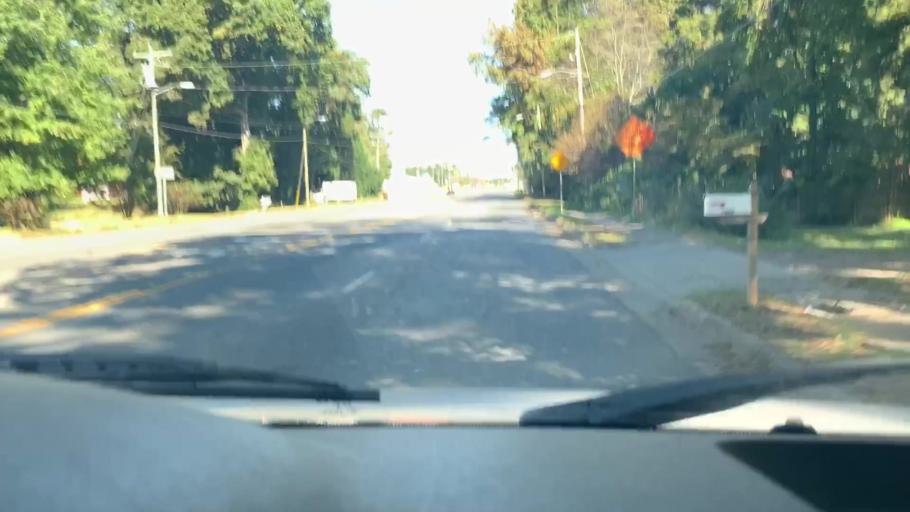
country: US
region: North Carolina
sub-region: Mecklenburg County
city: Charlotte
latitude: 35.2879
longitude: -80.7948
